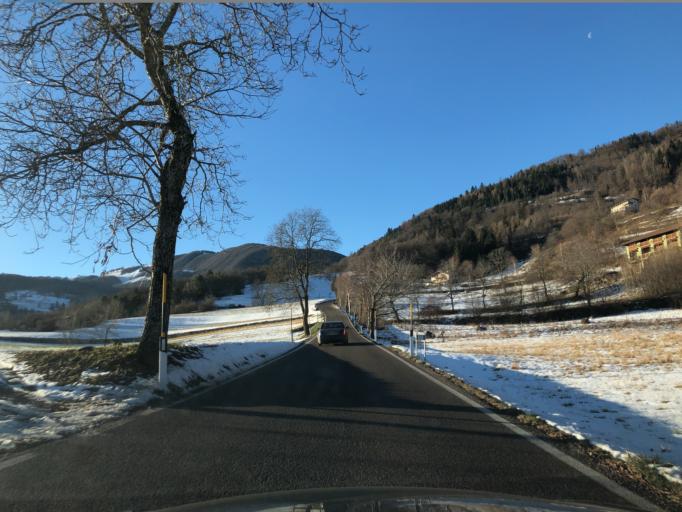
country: IT
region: Trentino-Alto Adige
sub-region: Provincia di Trento
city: Brentonico
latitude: 45.8102
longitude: 10.9419
